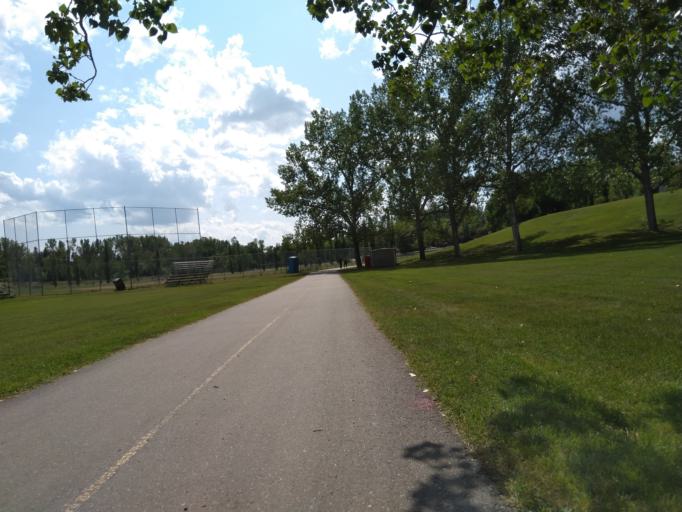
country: CA
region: Alberta
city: Calgary
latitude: 51.0813
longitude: -114.0771
